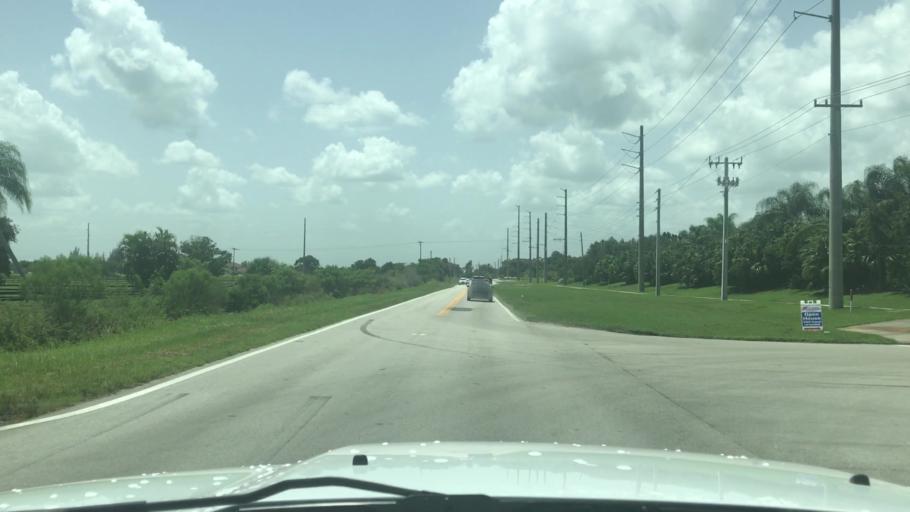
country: US
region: Florida
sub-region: Indian River County
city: Vero Beach South
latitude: 27.6241
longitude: -80.4428
